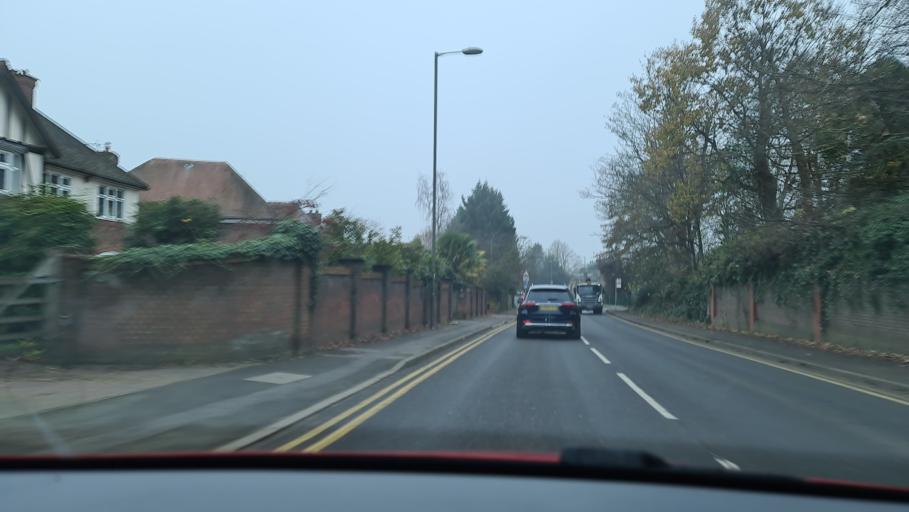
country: GB
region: England
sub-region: Surrey
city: Esher
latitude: 51.3651
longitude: -0.3639
